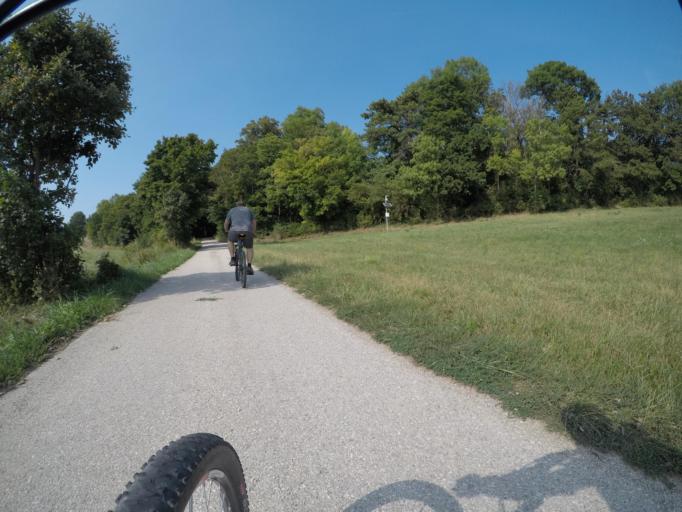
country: AT
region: Lower Austria
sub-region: Politischer Bezirk Baden
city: Berndorf
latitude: 47.9547
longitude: 16.1112
